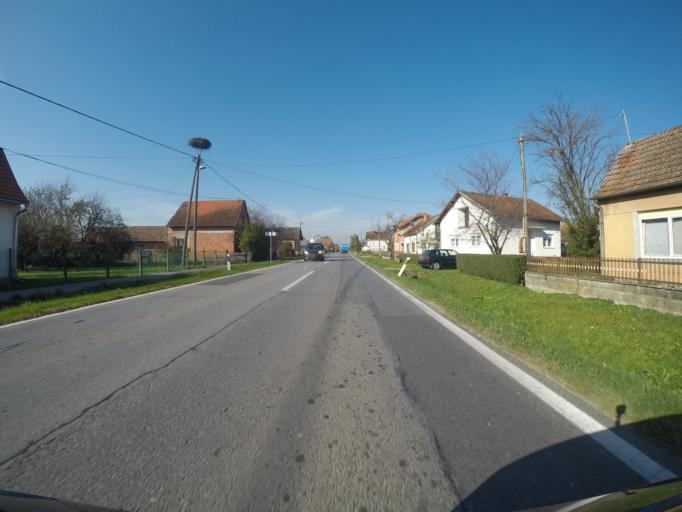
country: HR
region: Bjelovarsko-Bilogorska
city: Predavac
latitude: 45.9265
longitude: 16.7871
